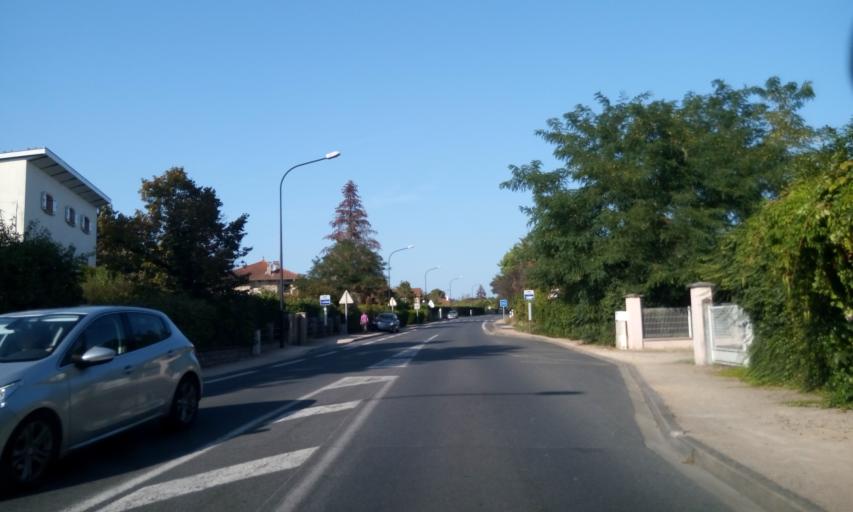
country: FR
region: Rhone-Alpes
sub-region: Departement du Rhone
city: Anse
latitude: 45.9450
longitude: 4.7381
